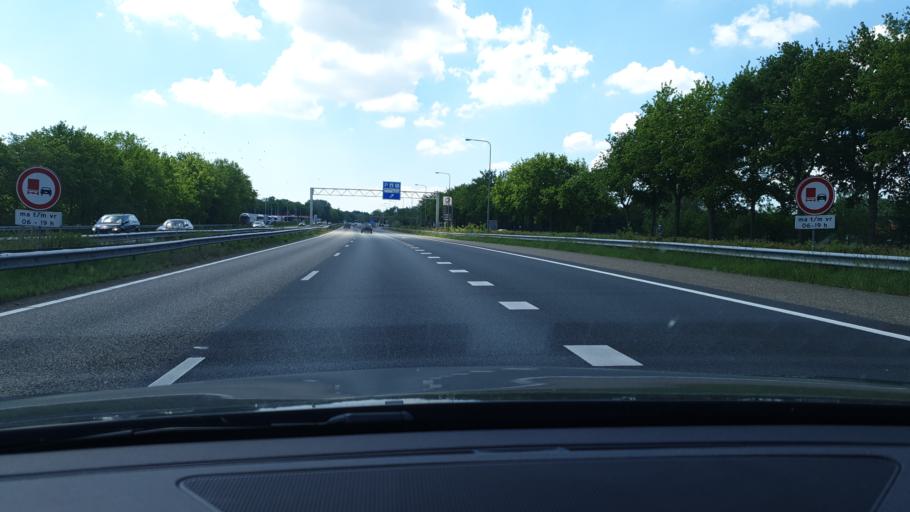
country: NL
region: North Brabant
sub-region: Gemeente Bergen op Zoom
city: Bergen op Zoom
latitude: 51.5069
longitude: 4.3562
